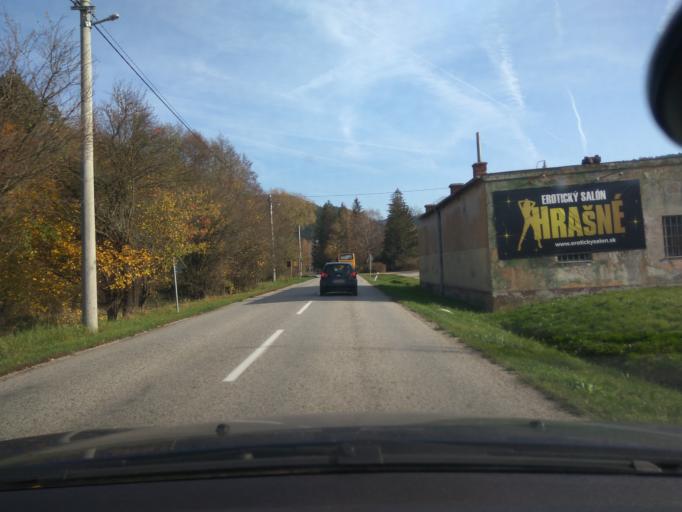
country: SK
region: Nitriansky
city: Brezova pod Bradlom
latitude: 48.6522
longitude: 17.5285
